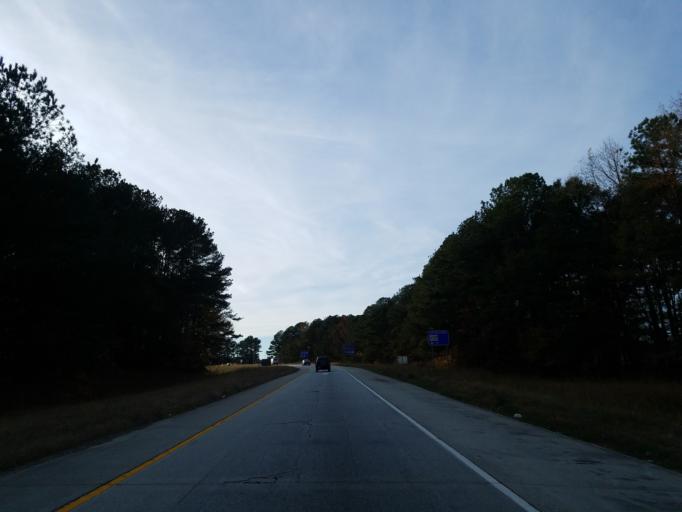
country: US
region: Georgia
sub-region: Carroll County
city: Temple
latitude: 33.7179
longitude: -85.0249
